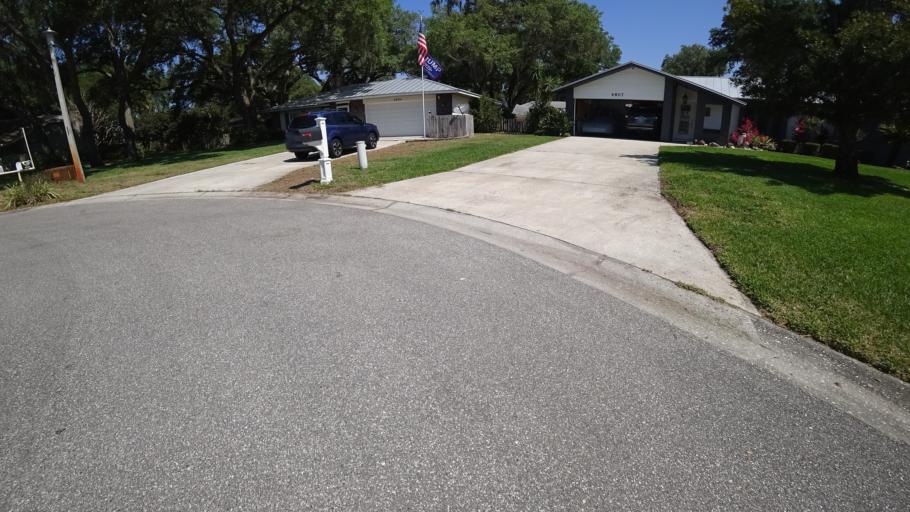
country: US
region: Florida
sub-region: Manatee County
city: Samoset
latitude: 27.4531
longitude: -82.5242
